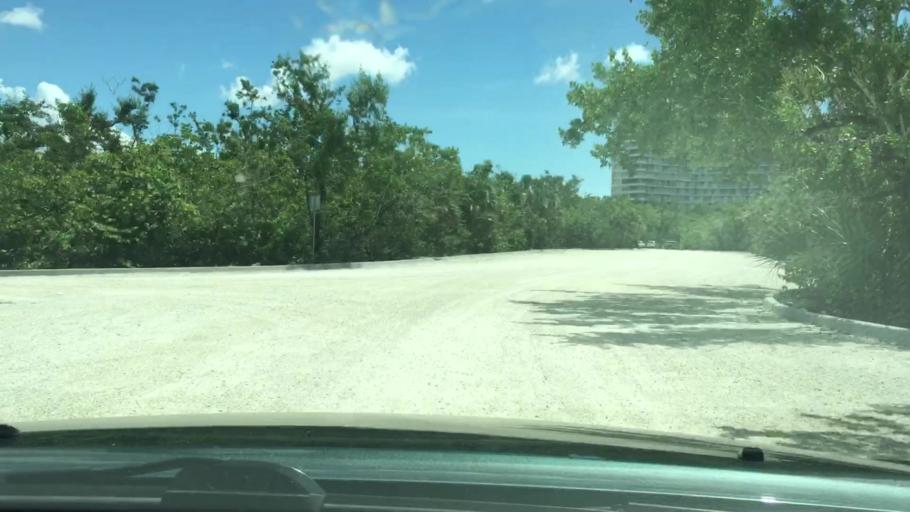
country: US
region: Florida
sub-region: Collier County
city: Marco
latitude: 25.9481
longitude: -81.7423
